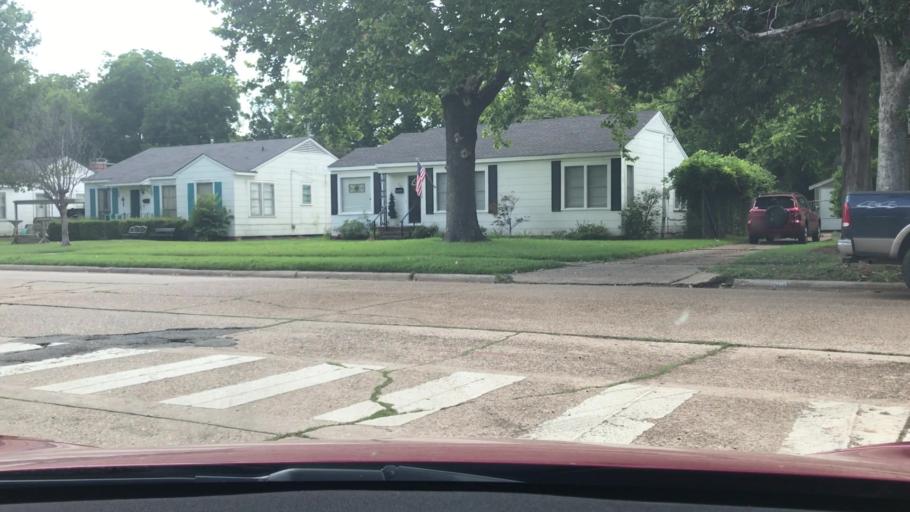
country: US
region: Louisiana
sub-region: Bossier Parish
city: Bossier City
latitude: 32.4597
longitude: -93.7193
